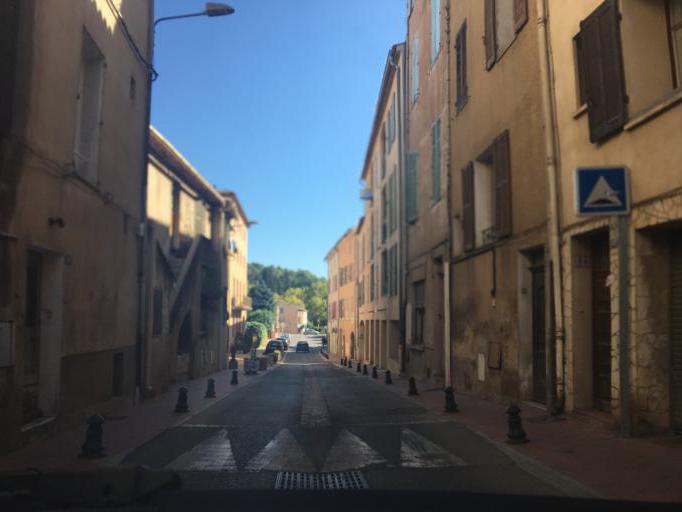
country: FR
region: Provence-Alpes-Cote d'Azur
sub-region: Departement du Var
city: Salernes
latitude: 43.5627
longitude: 6.2326
